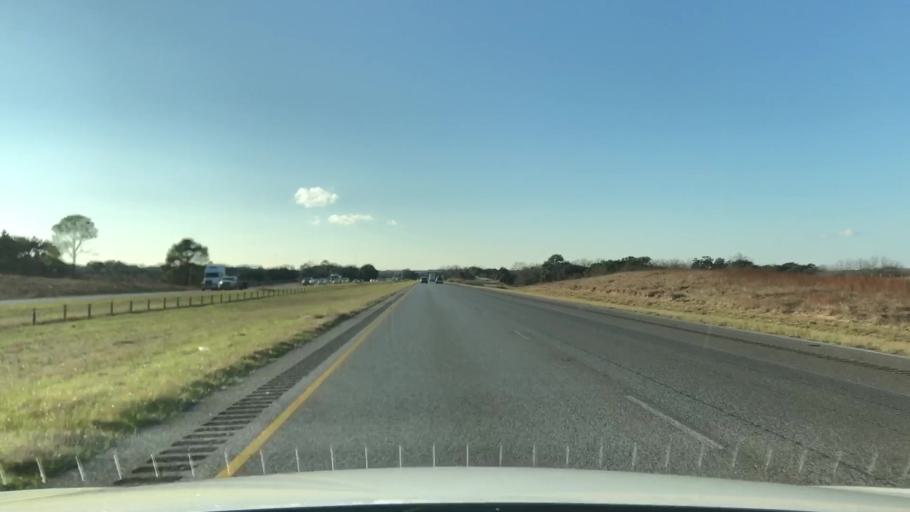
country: US
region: Texas
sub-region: Fayette County
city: Flatonia
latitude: 29.6949
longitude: -97.0261
